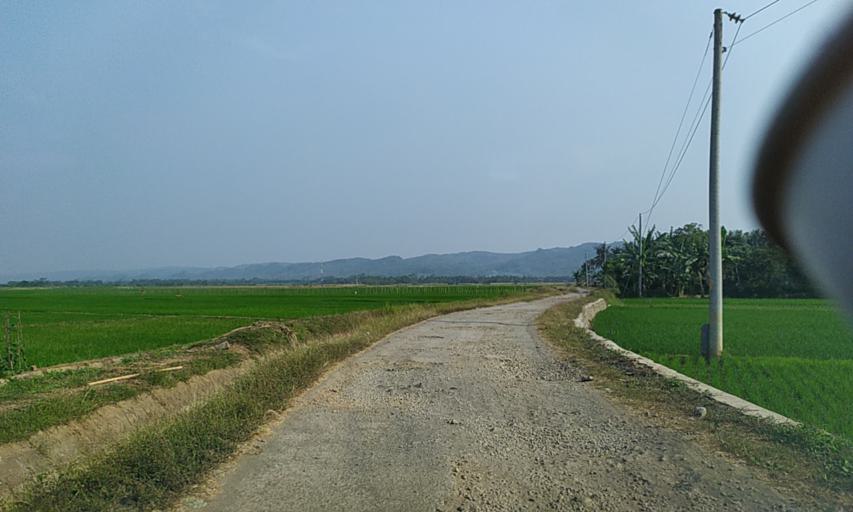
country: ID
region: Central Java
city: Mulyadadi
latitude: -7.3397
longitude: 108.7558
